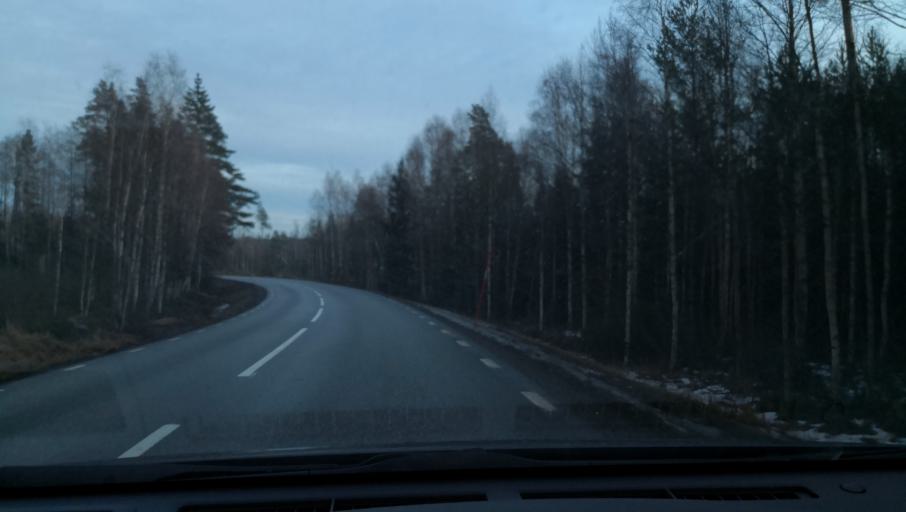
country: SE
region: OErebro
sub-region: Degerfors Kommun
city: Degerfors
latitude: 59.1372
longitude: 14.4418
